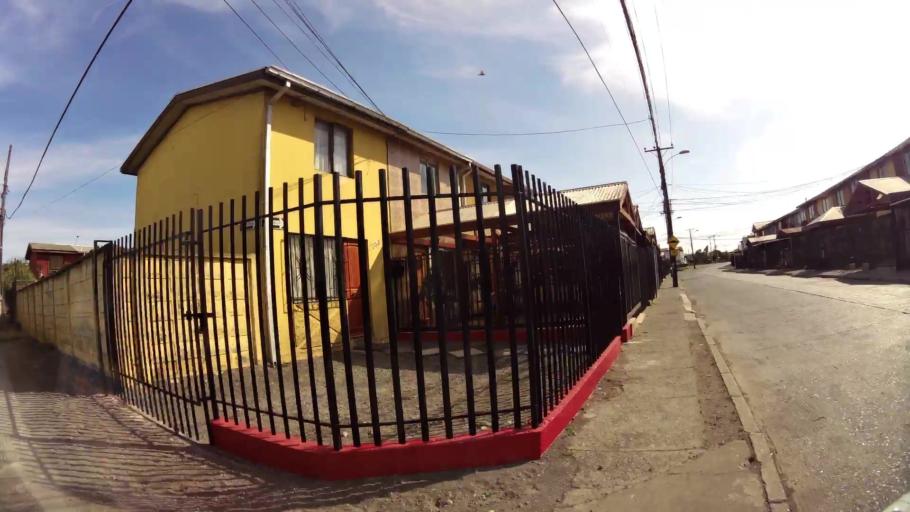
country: CL
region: Biobio
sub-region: Provincia de Concepcion
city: Talcahuano
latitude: -36.7904
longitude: -73.1134
